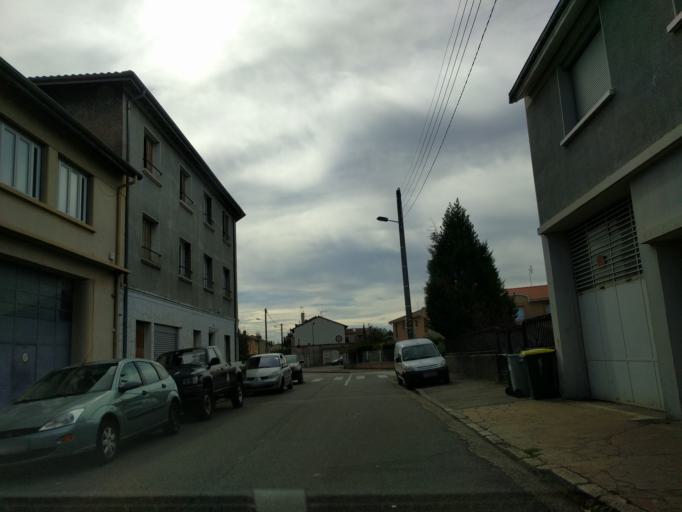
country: FR
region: Rhone-Alpes
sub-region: Departement du Rhone
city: Villeurbanne
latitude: 45.7547
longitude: 4.9040
